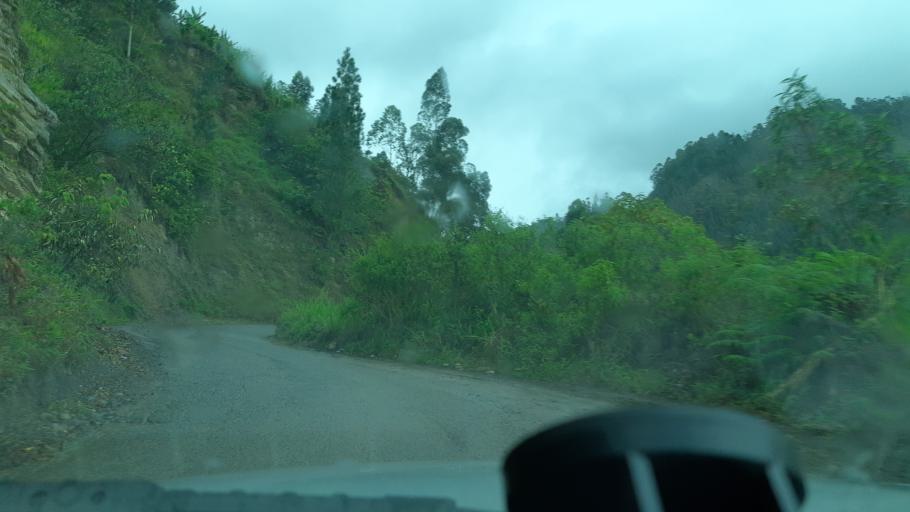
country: CO
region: Boyaca
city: Chinavita
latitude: 5.2172
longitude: -73.3934
